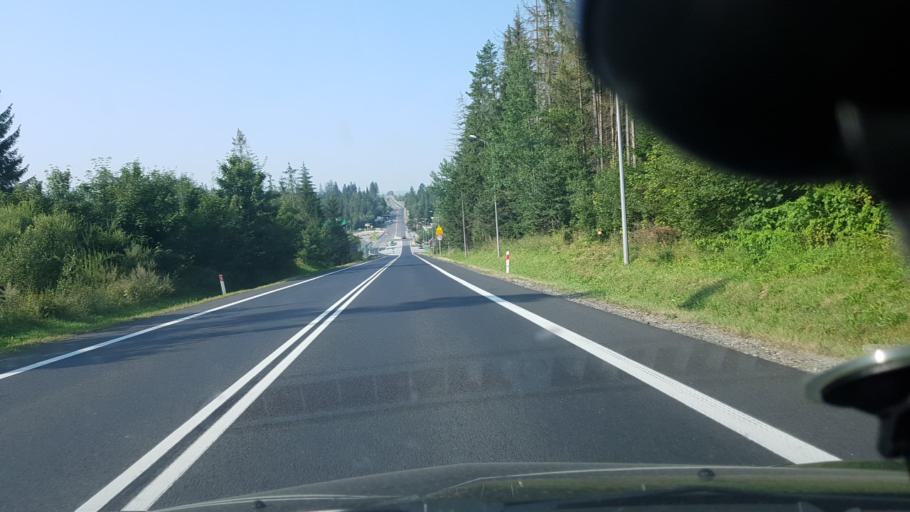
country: PL
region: Lesser Poland Voivodeship
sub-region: Powiat nowotarski
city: Chyzne
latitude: 49.4102
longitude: 19.6609
